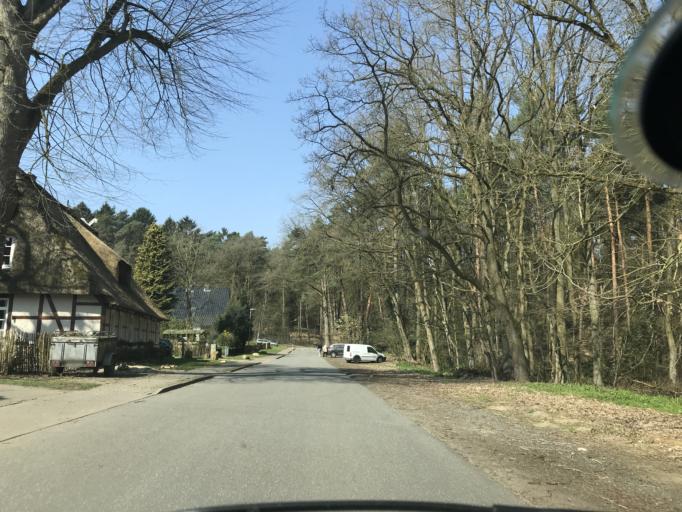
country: DE
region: Lower Saxony
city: Buxtehude
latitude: 53.4507
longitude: 9.7303
